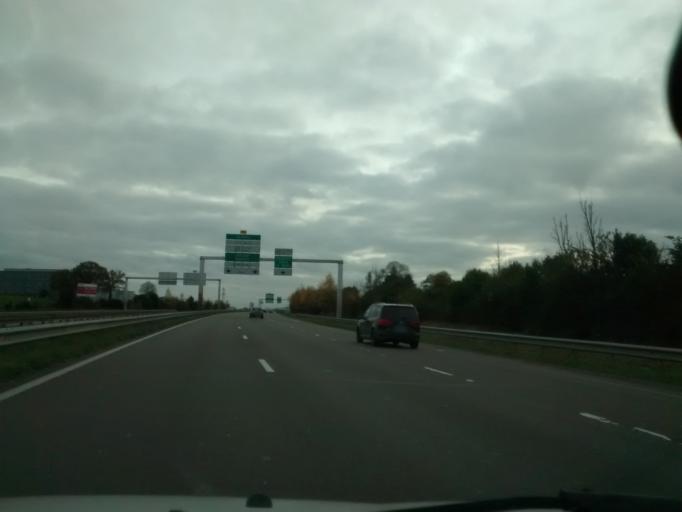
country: FR
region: Brittany
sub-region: Departement d'Ille-et-Vilaine
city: Saint-Gregoire
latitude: 48.1504
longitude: -1.6998
